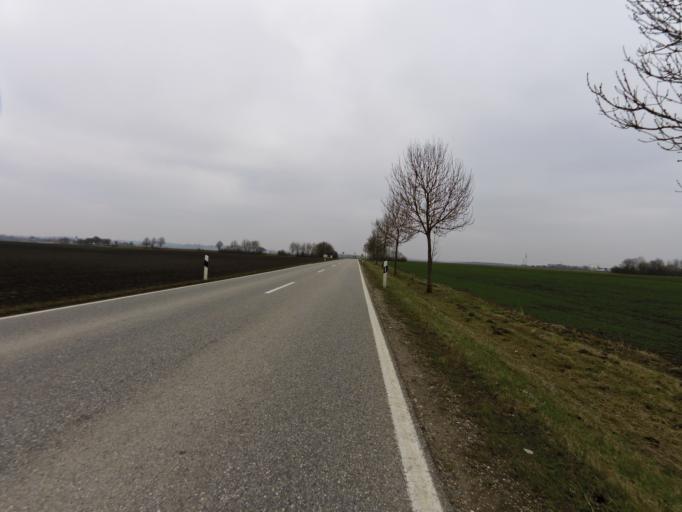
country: DE
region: Bavaria
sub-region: Upper Bavaria
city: Berglern
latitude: 48.4091
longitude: 11.9168
